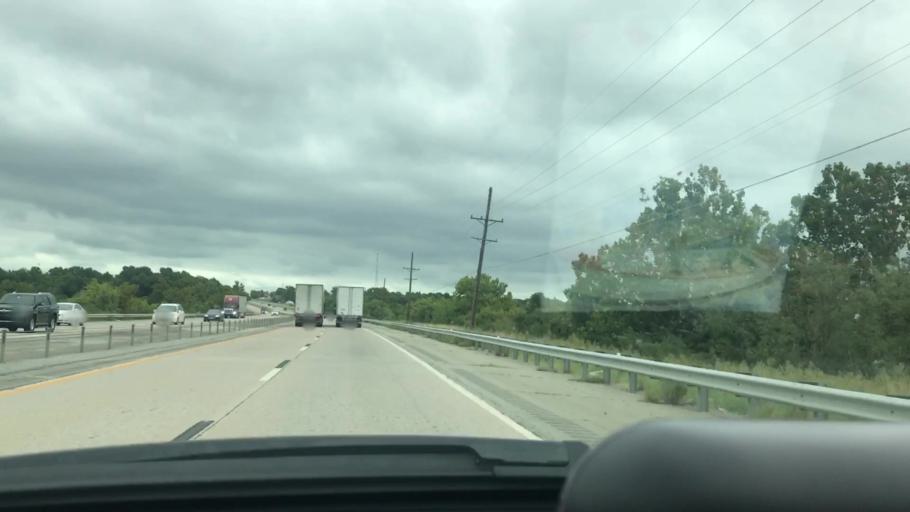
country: US
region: Oklahoma
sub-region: McIntosh County
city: Eufaula
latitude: 35.3480
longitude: -95.5799
